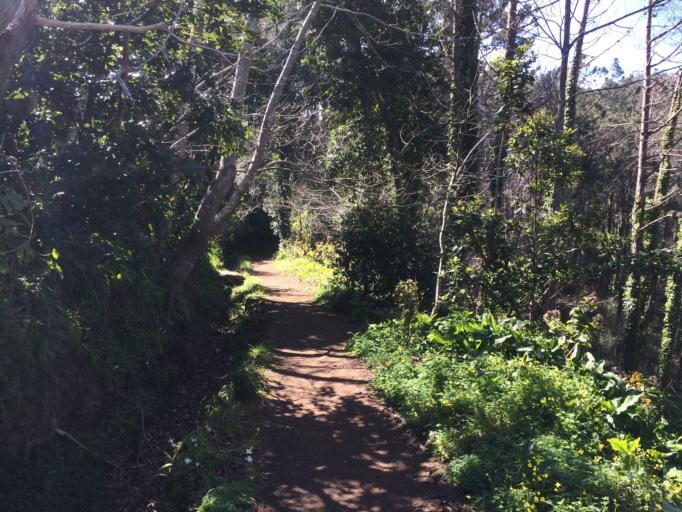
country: PT
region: Madeira
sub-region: Santa Cruz
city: Camacha
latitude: 32.6806
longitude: -16.8556
